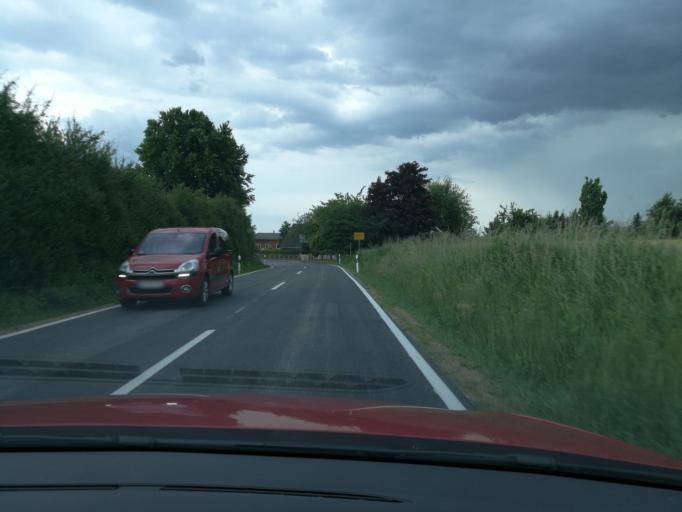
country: DE
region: Schleswig-Holstein
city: Lasbek
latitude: 53.7317
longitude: 10.3620
